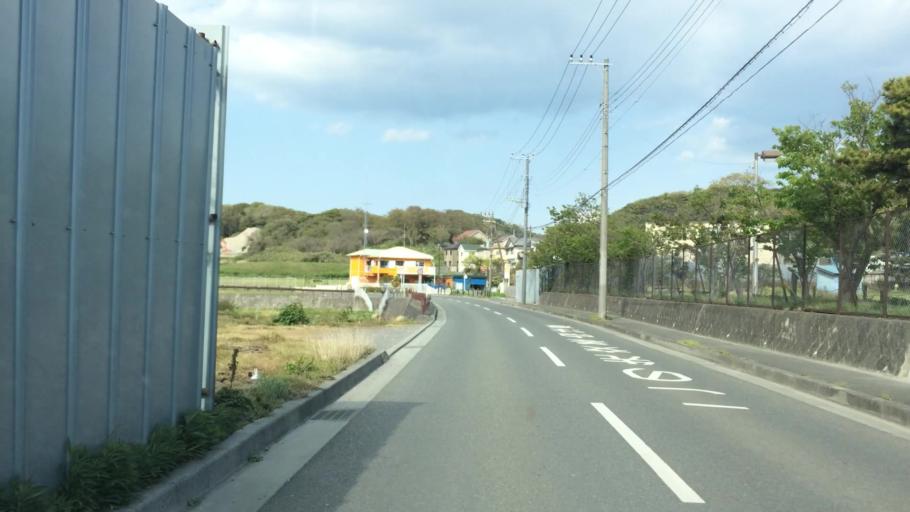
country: JP
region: Kanagawa
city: Yokosuka
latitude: 35.2301
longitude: 139.6297
